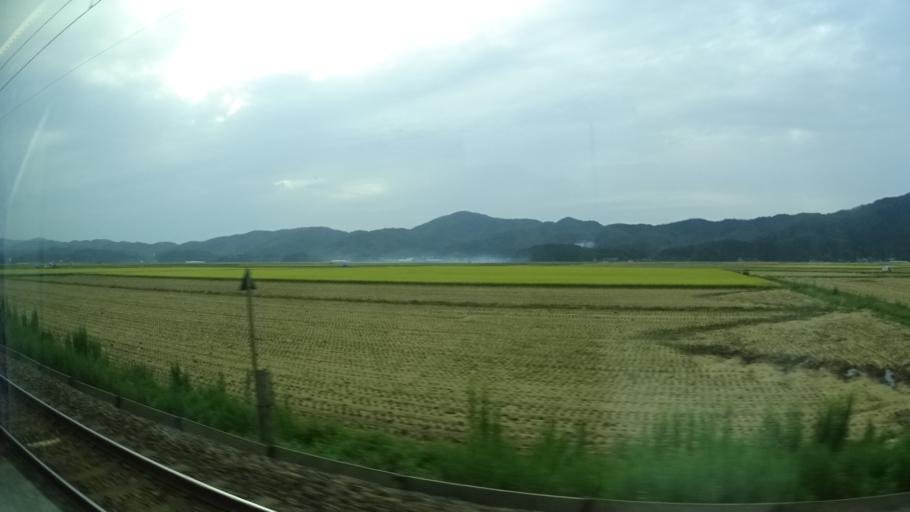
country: JP
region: Yamagata
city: Tsuruoka
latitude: 38.7309
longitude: 139.7491
